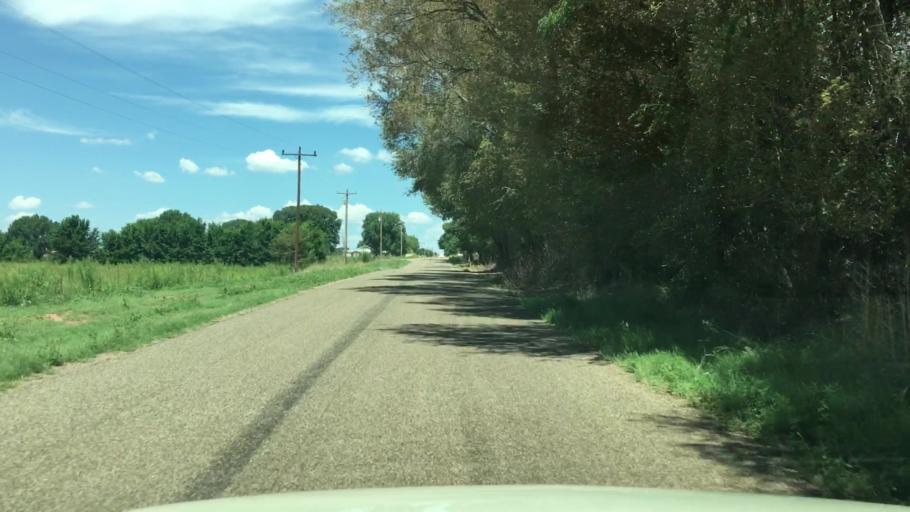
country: US
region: New Mexico
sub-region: De Baca County
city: Fort Sumner
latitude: 34.4381
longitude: -104.1936
